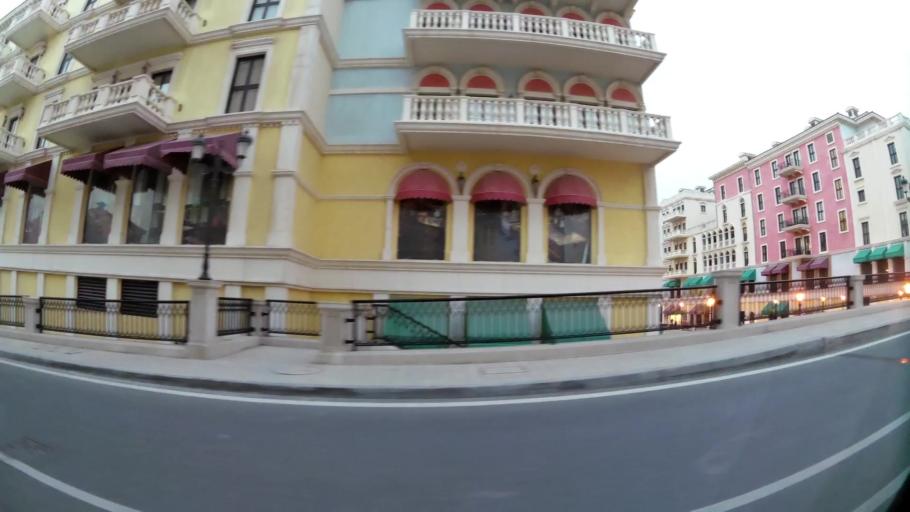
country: QA
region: Baladiyat ad Dawhah
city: Doha
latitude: 25.3771
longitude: 51.5436
